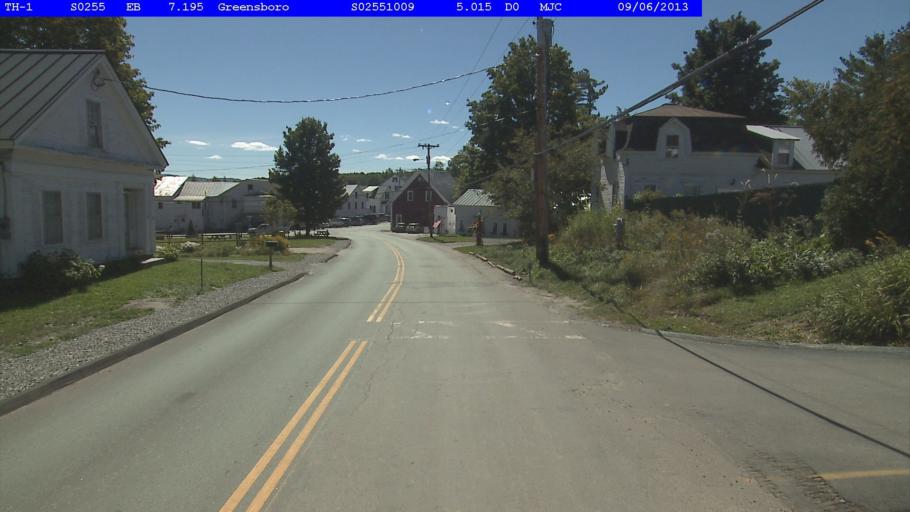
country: US
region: Vermont
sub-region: Caledonia County
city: Hardwick
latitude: 44.5766
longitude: -72.2960
